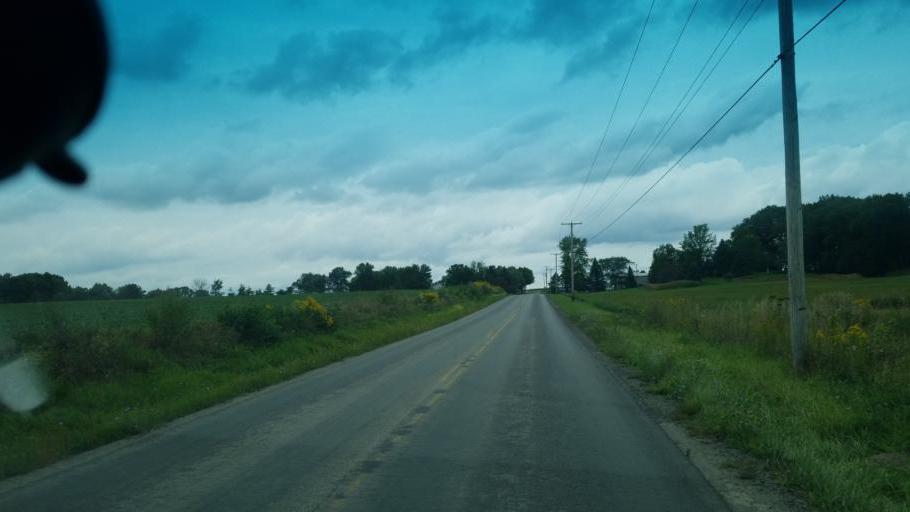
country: US
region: Ohio
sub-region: Huron County
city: Plymouth
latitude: 40.9671
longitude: -82.5835
